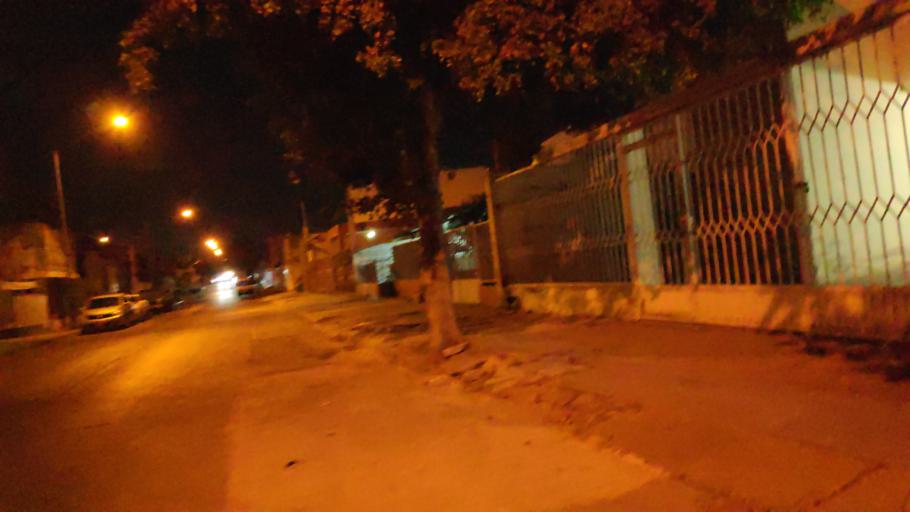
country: MX
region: Sinaloa
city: Culiacan
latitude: 24.7924
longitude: -107.4104
